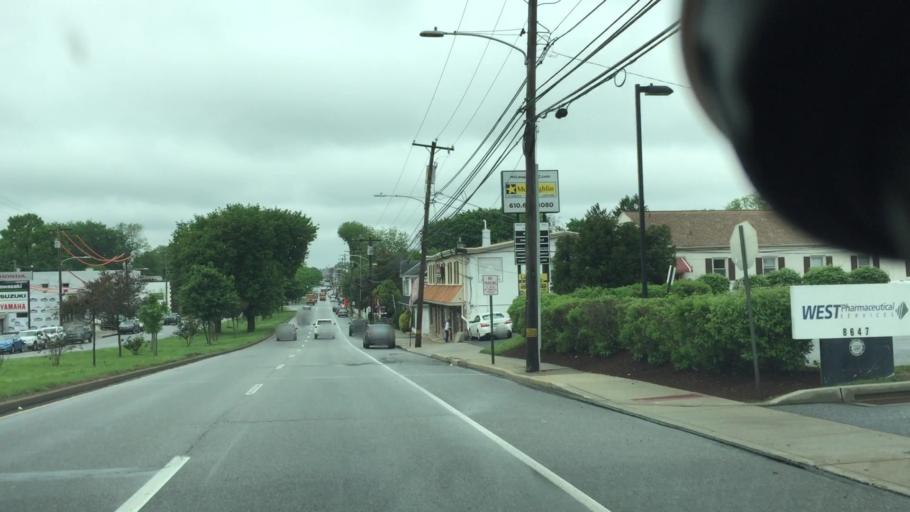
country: US
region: Pennsylvania
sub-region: Delaware County
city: Drexel Hill
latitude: 39.9671
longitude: -75.2861
